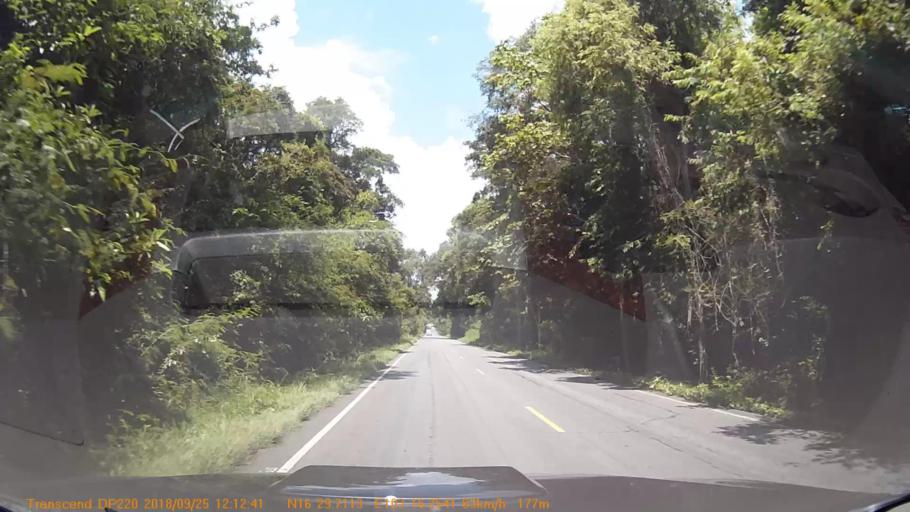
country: TH
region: Kalasin
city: Huai Mek
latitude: 16.4952
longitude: 103.2709
